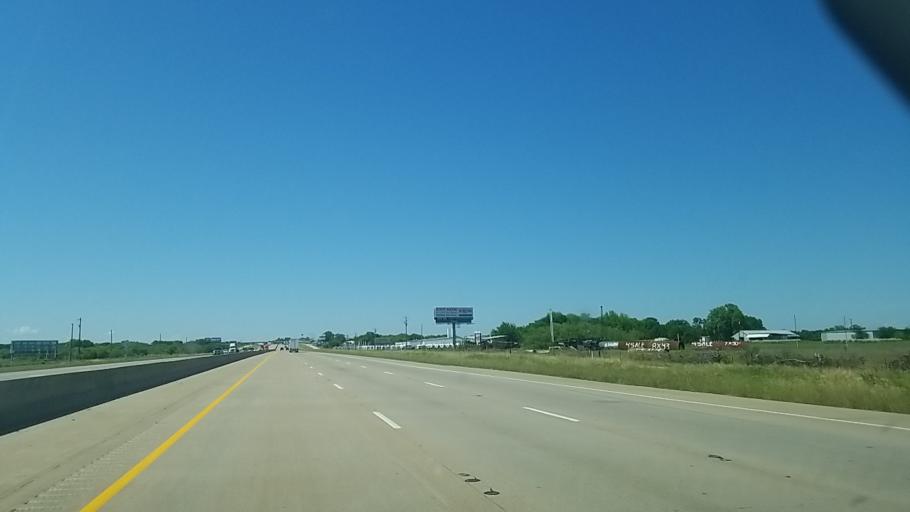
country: US
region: Texas
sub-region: Navarro County
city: Corsicana
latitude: 32.1868
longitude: -96.4722
